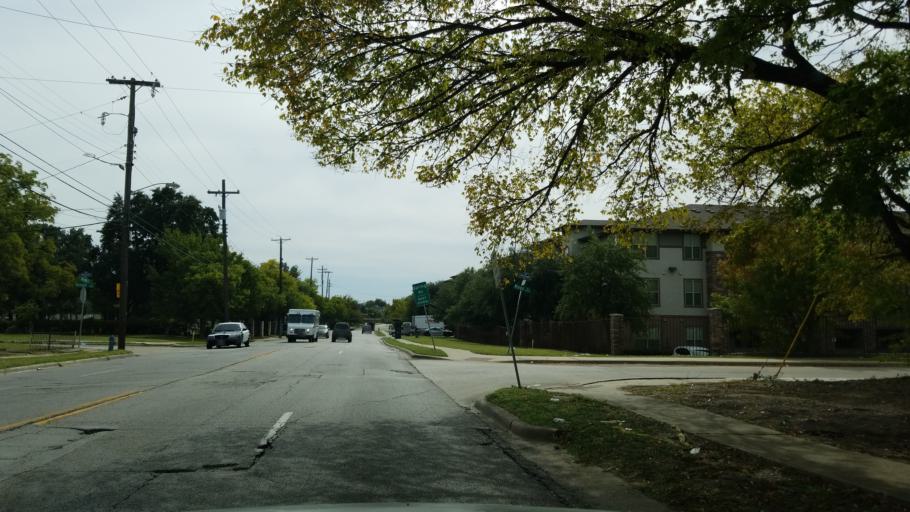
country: US
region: Texas
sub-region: Dallas County
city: Dallas
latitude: 32.7808
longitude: -96.7377
